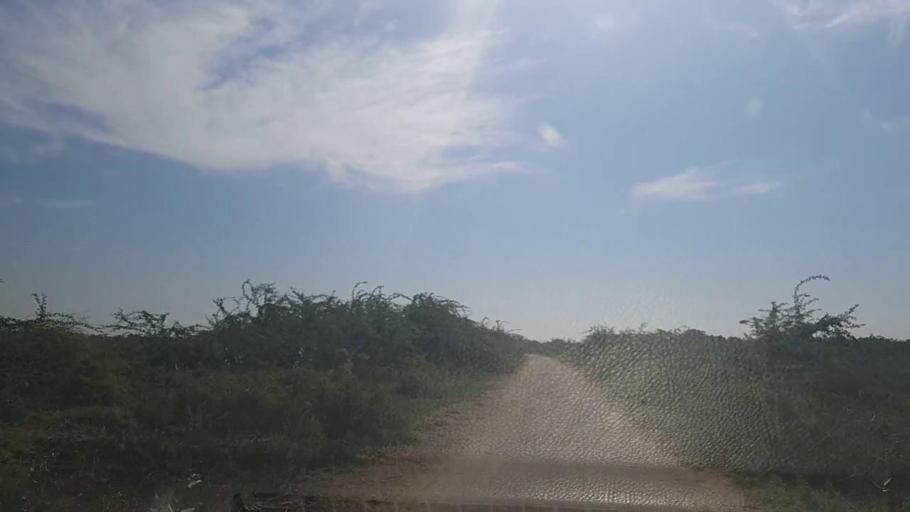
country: PK
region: Sindh
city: Mirpur Batoro
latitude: 24.6676
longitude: 68.1840
